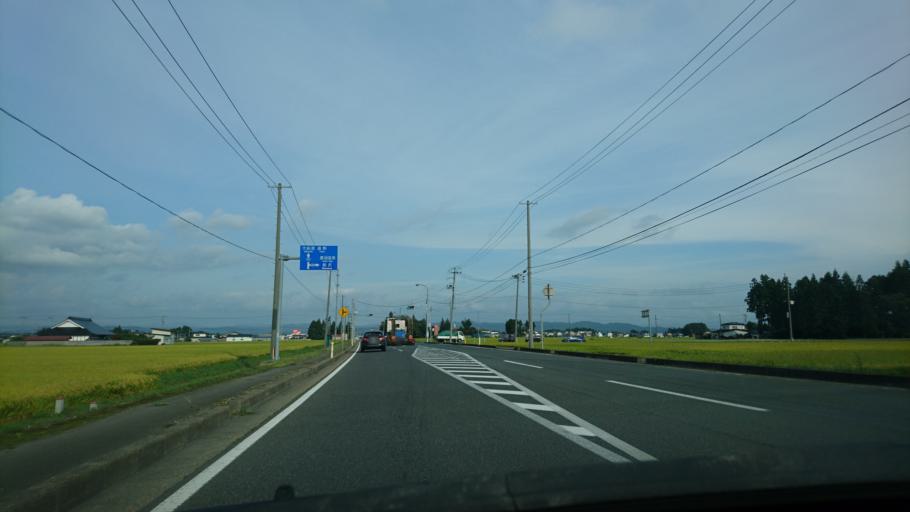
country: JP
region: Iwate
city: Kitakami
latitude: 39.3018
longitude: 141.0531
